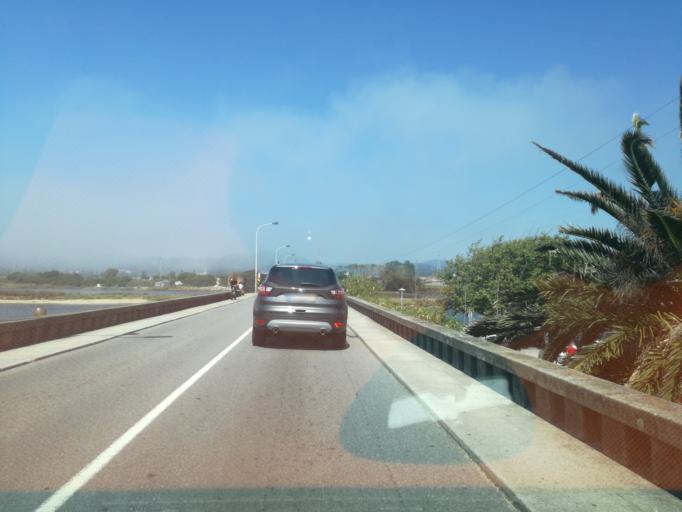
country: PT
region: Braga
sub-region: Esposende
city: Esposende
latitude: 41.5143
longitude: -8.7731
